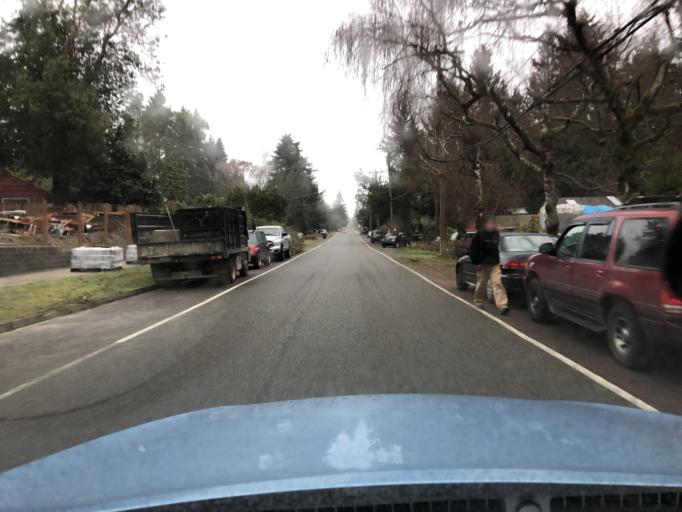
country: US
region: Washington
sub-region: King County
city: Lake Forest Park
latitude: 47.7356
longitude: -122.2992
